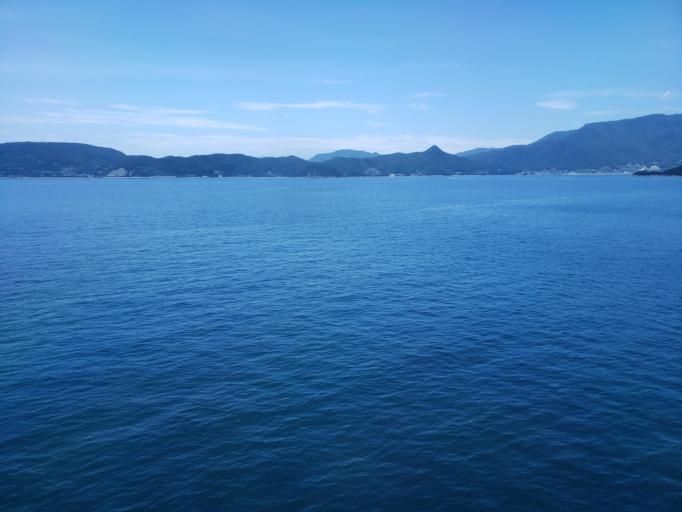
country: JP
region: Kagawa
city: Tonosho
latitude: 34.4293
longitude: 134.2813
